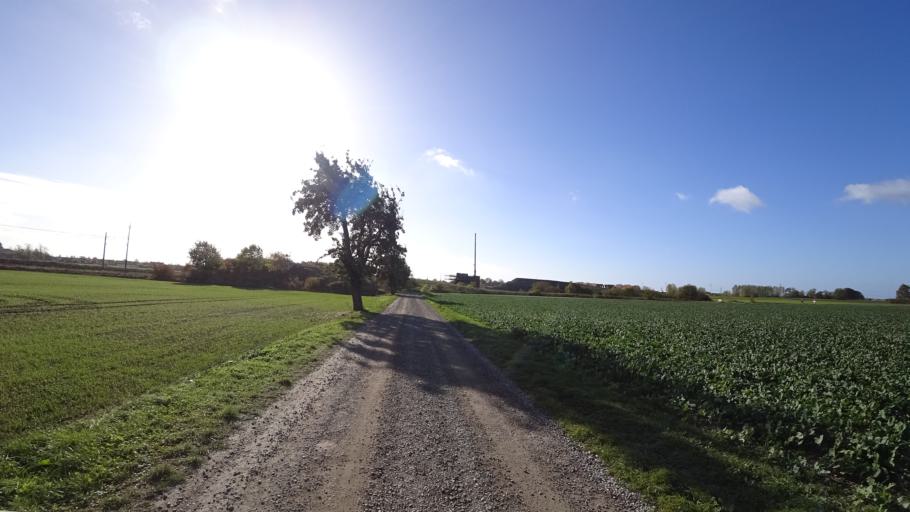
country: SE
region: Skane
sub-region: Staffanstorps Kommun
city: Hjaerup
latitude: 55.6796
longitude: 13.1440
